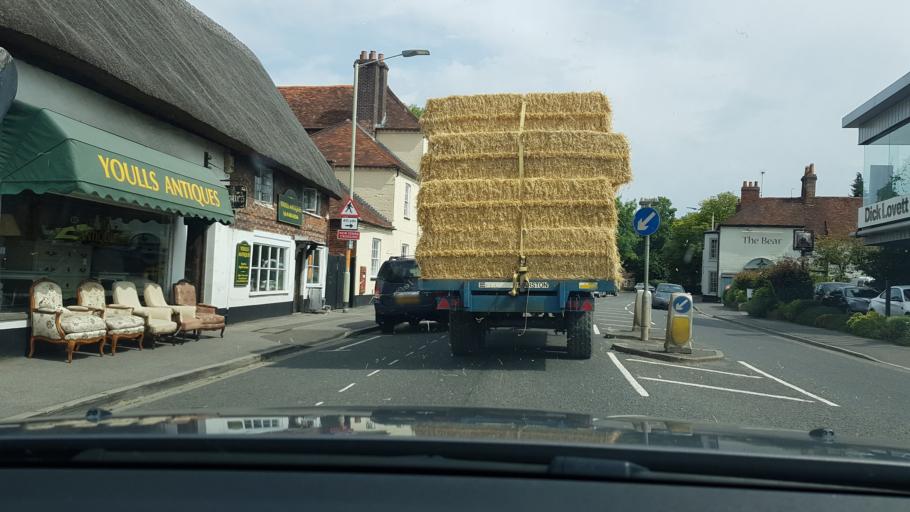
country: GB
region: England
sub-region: West Berkshire
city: Hungerford
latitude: 51.4176
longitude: -1.5189
